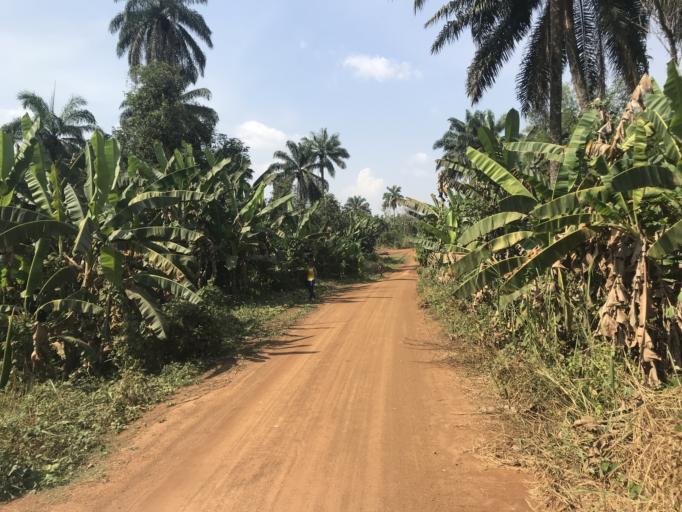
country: NG
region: Osun
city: Osu
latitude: 7.6401
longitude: 4.6589
